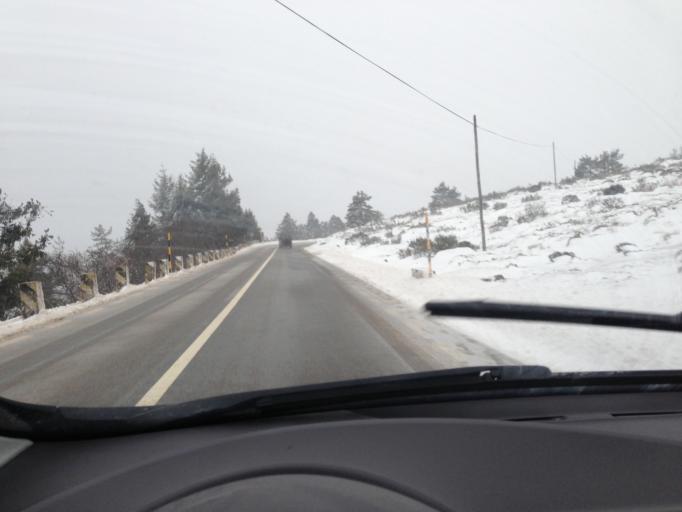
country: PT
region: Castelo Branco
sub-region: Covilha
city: Covilha
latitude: 40.3133
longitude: -7.5560
